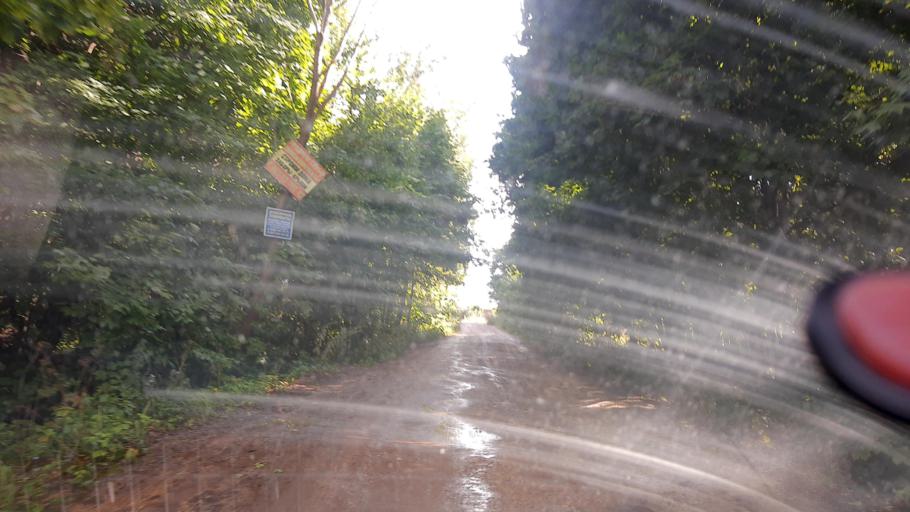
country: RU
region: Bashkortostan
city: Iglino
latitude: 54.7695
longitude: 56.4535
